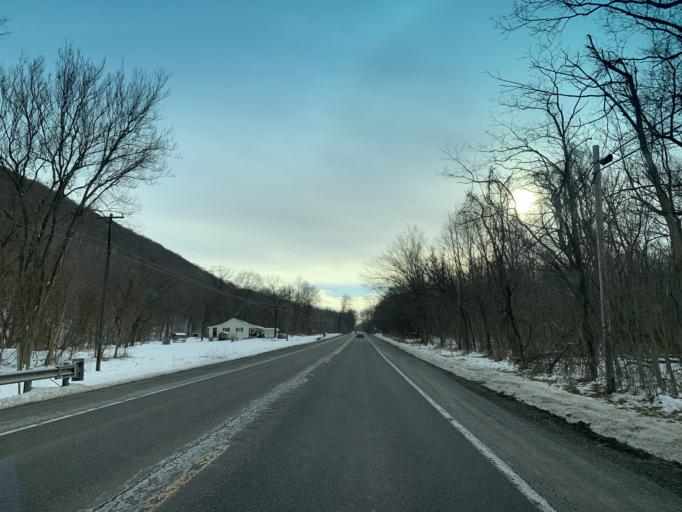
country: US
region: Maryland
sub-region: Allegany County
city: Bel Air
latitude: 39.5261
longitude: -78.9024
